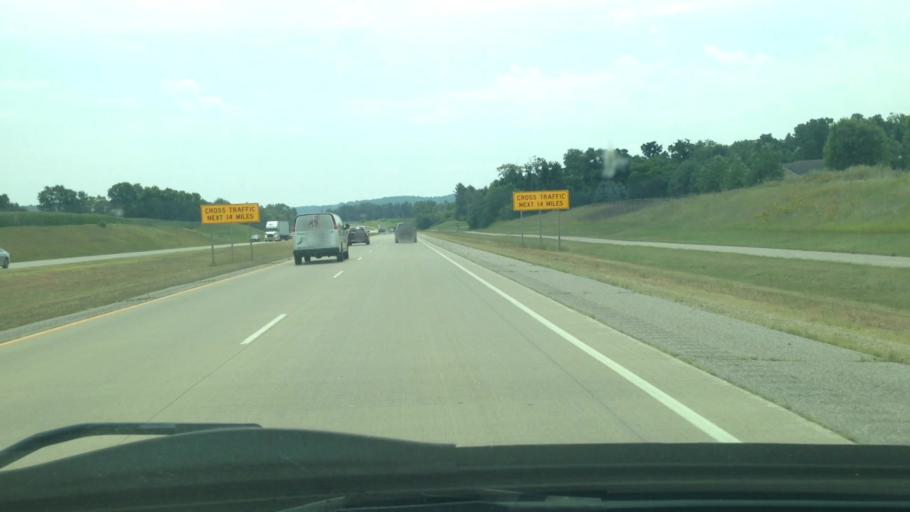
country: US
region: Wisconsin
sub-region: Sauk County
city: Sauk City
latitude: 43.2594
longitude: -89.7097
